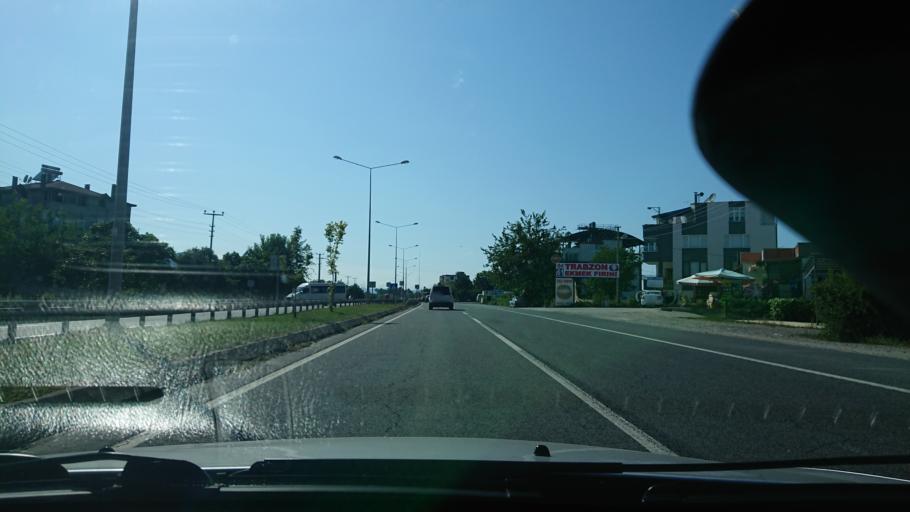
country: TR
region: Ordu
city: Unieh
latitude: 41.1048
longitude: 37.3873
